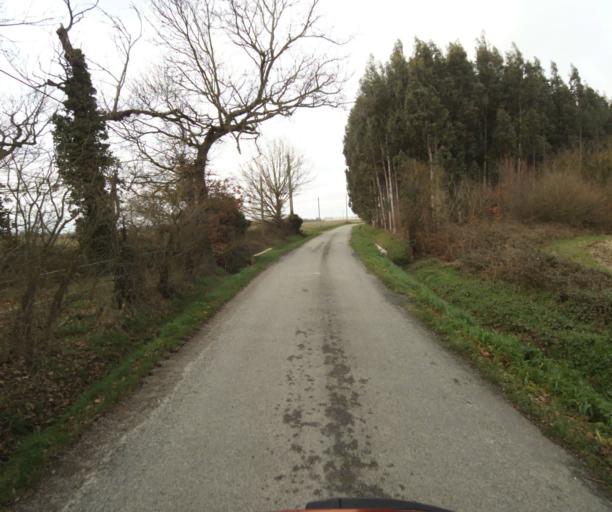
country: FR
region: Midi-Pyrenees
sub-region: Departement de l'Ariege
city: Mazeres
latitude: 43.2026
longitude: 1.6702
